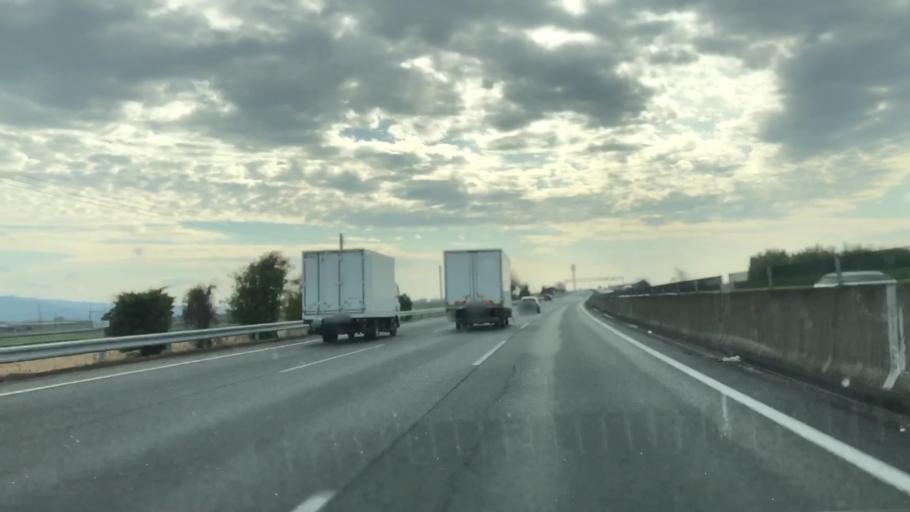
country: JP
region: Saga Prefecture
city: Tosu
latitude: 33.3609
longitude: 130.5405
